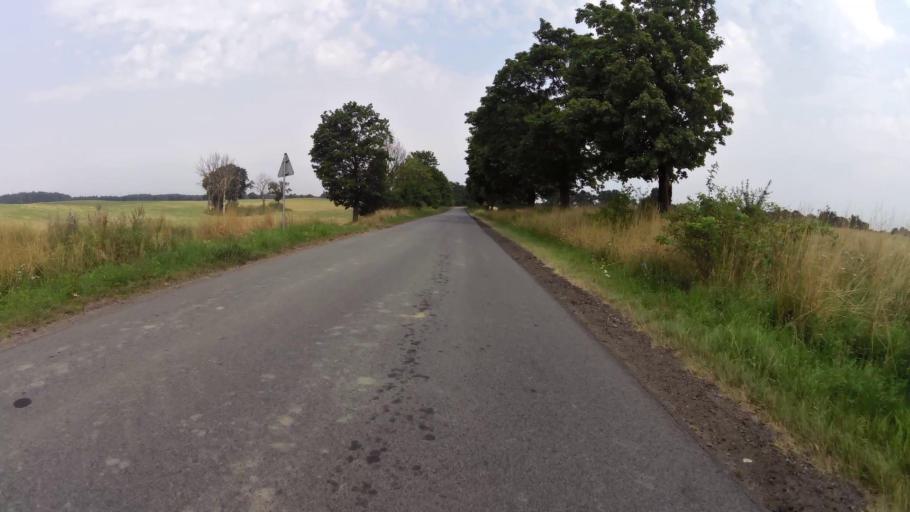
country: PL
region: West Pomeranian Voivodeship
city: Trzcinsko Zdroj
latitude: 52.9172
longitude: 14.6497
